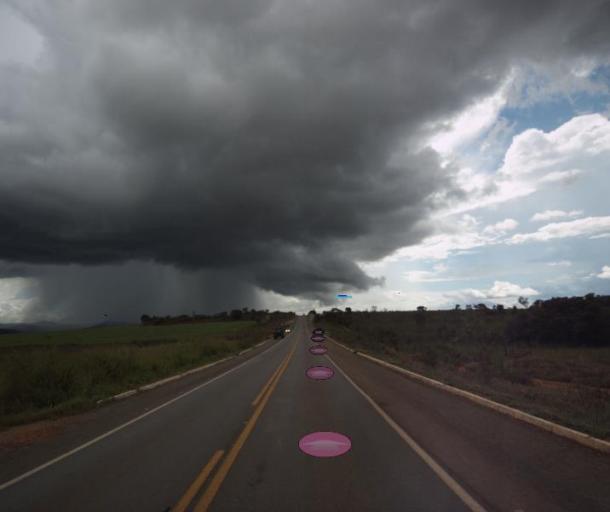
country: BR
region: Goias
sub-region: Uruacu
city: Uruacu
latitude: -14.6587
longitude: -49.1589
